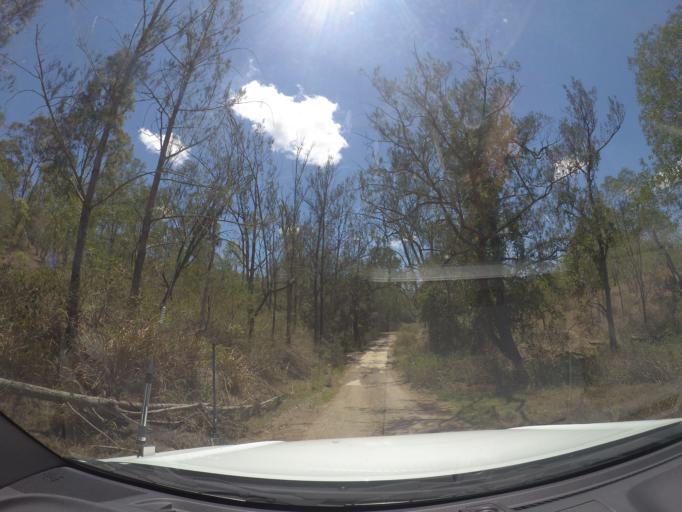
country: AU
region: Queensland
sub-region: Ipswich
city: Springfield Lakes
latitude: -27.8184
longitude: 152.8466
